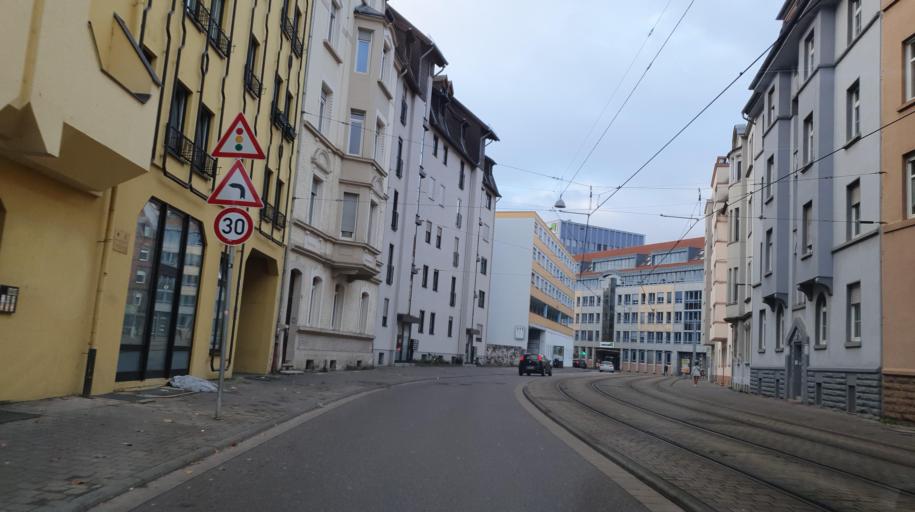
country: DE
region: Saarland
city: Saarbrucken
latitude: 49.2303
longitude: 7.0087
